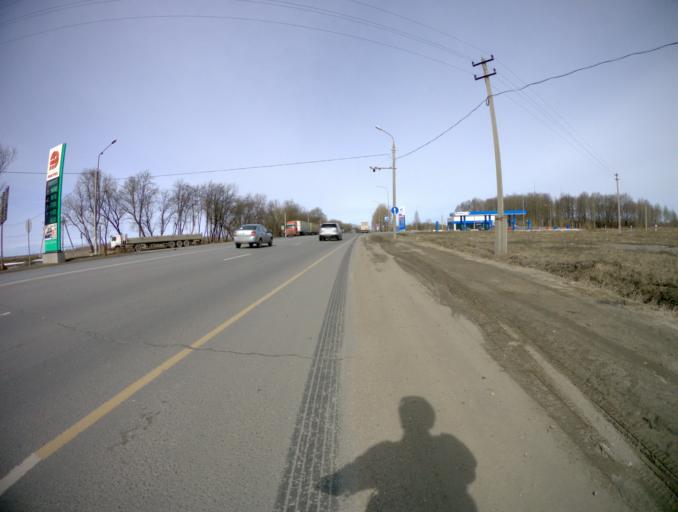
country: RU
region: Vladimir
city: Kommunar
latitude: 56.1775
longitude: 40.4549
